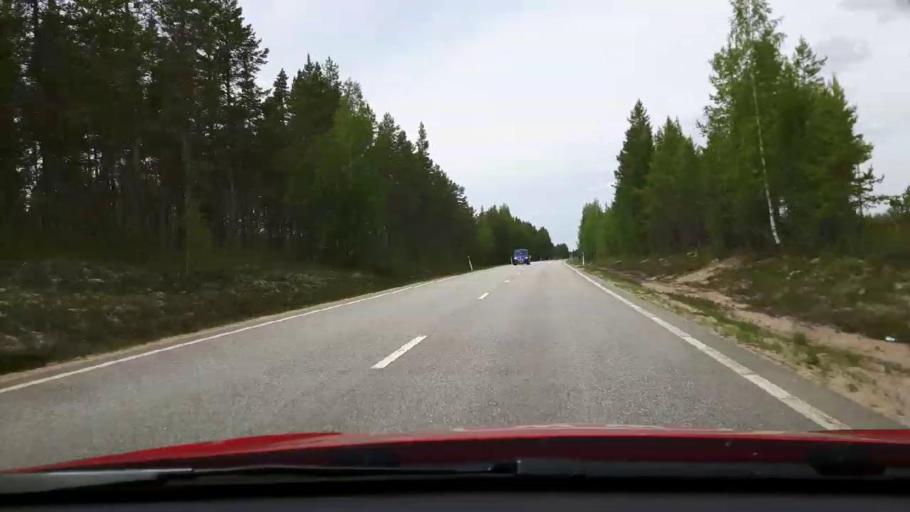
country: SE
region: Jaemtland
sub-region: Harjedalens Kommun
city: Sveg
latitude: 62.1134
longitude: 14.1809
